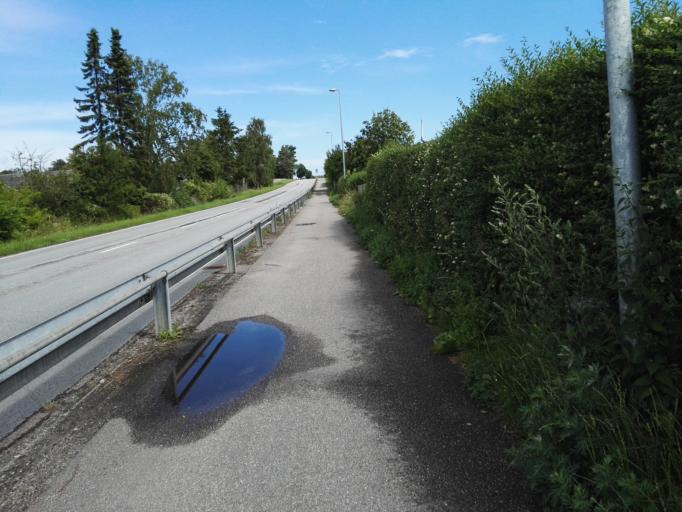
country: DK
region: Capital Region
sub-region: Egedal Kommune
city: Olstykke
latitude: 55.8015
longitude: 12.1610
